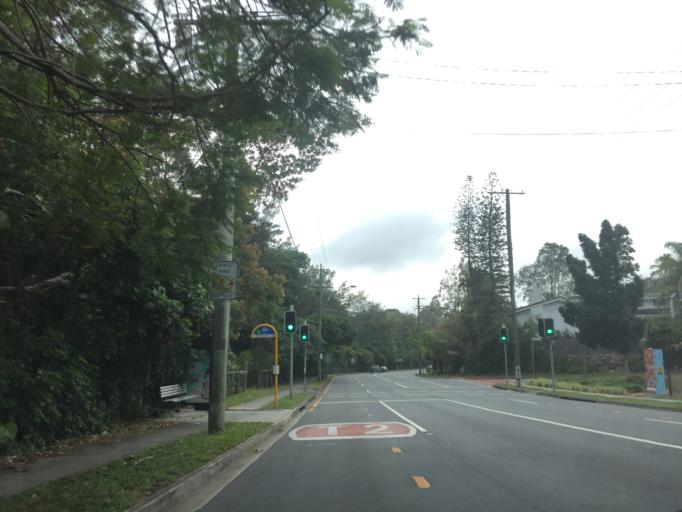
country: AU
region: Queensland
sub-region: Brisbane
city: Milton
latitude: -27.4482
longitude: 152.9718
